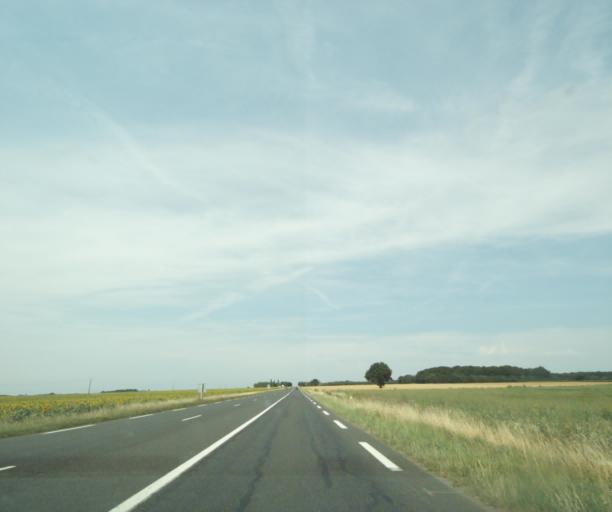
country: FR
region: Centre
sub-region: Departement d'Indre-et-Loire
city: Sainte-Maure-de-Touraine
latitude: 47.1649
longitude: 0.6505
